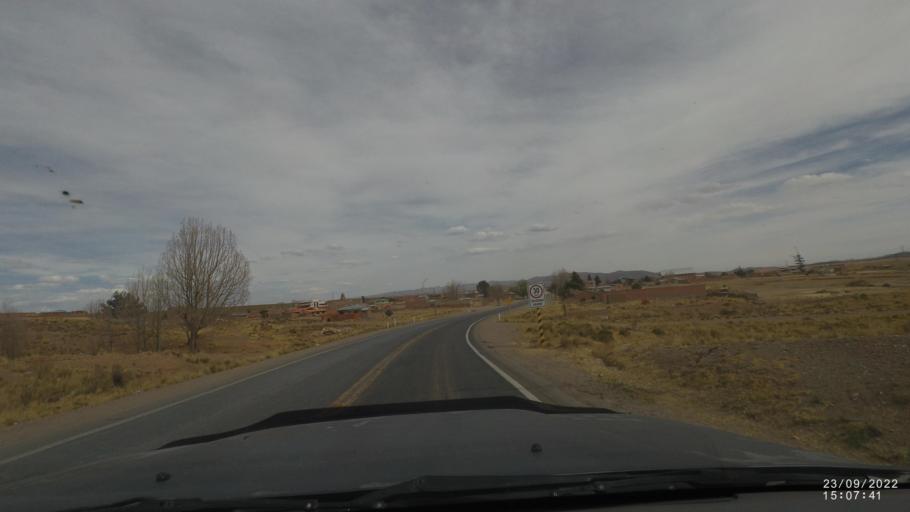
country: BO
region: Oruro
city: Oruro
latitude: -17.7609
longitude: -67.0301
